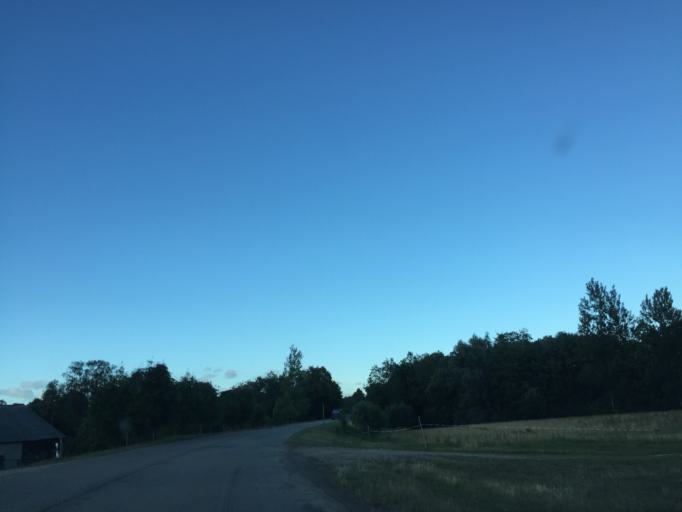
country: LV
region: Plavinu
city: Plavinas
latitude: 56.6069
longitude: 25.7934
